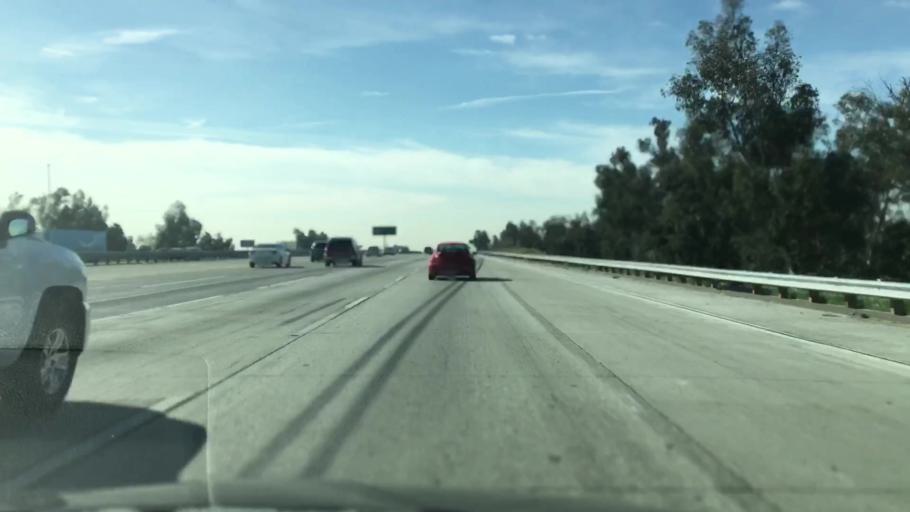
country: US
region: California
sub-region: San Bernardino County
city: Rancho Cucamonga
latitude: 34.1156
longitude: -117.5213
